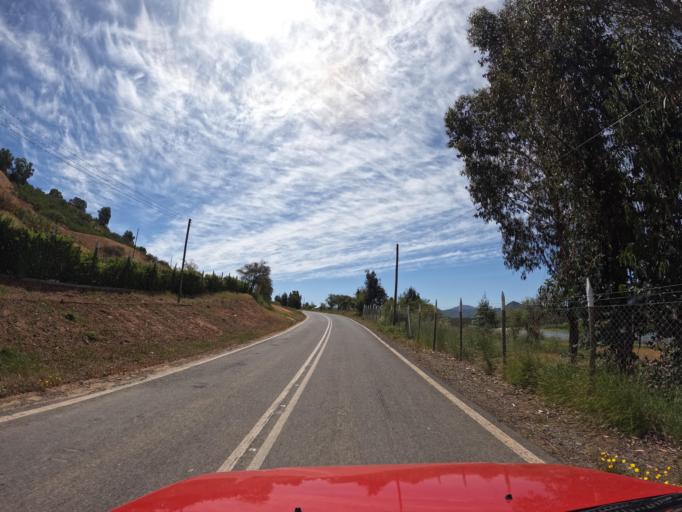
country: CL
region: Maule
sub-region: Provincia de Talca
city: Talca
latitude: -35.0419
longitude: -71.7526
